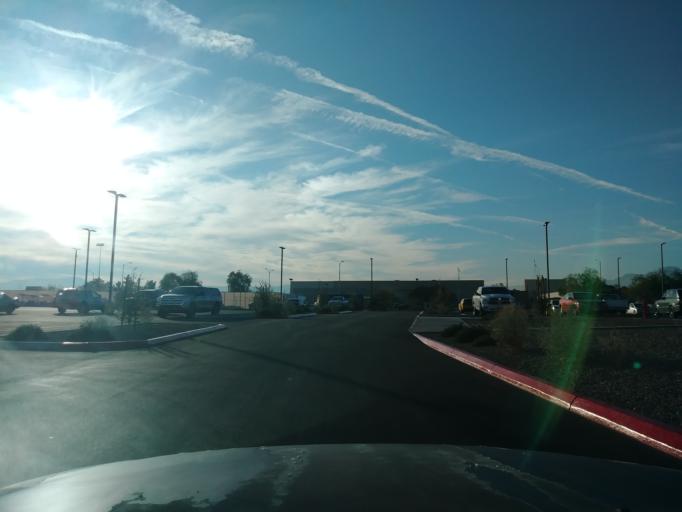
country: US
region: Nevada
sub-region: Clark County
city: Spring Valley
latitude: 36.1549
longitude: -115.2332
